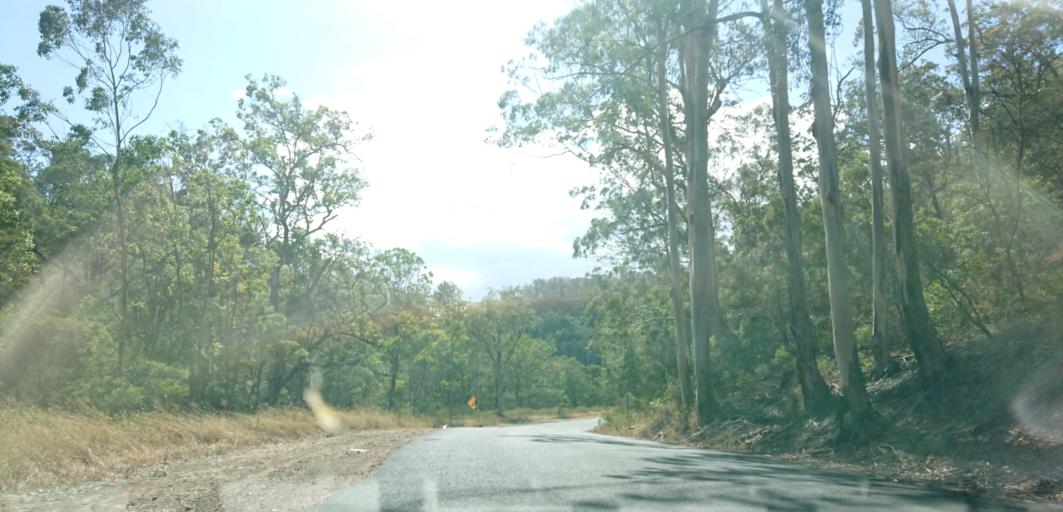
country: AU
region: Queensland
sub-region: Toowoomba
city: Top Camp
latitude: -27.7713
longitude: 152.0894
